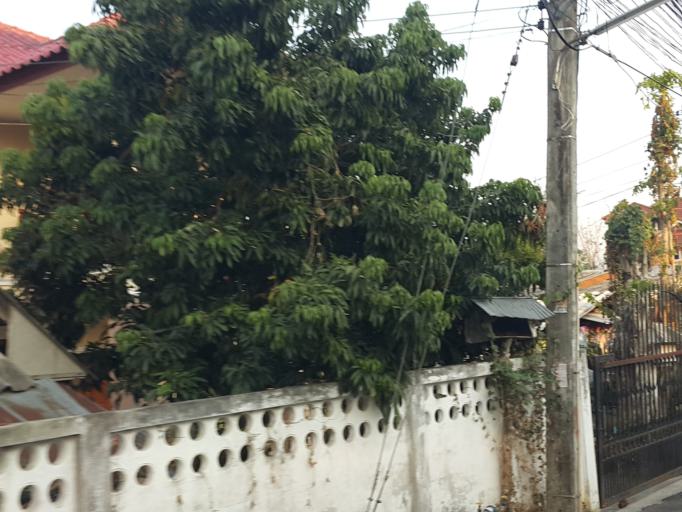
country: TH
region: Chiang Mai
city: San Sai
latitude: 18.9032
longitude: 98.9533
